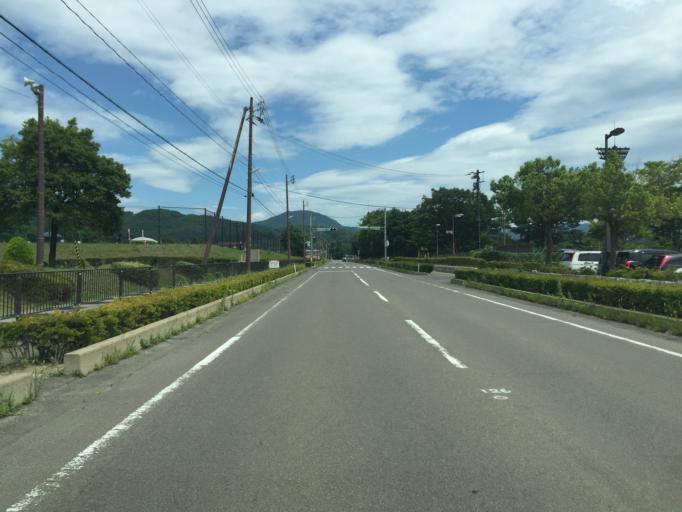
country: JP
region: Fukushima
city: Fukushima-shi
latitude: 37.8155
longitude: 140.4149
